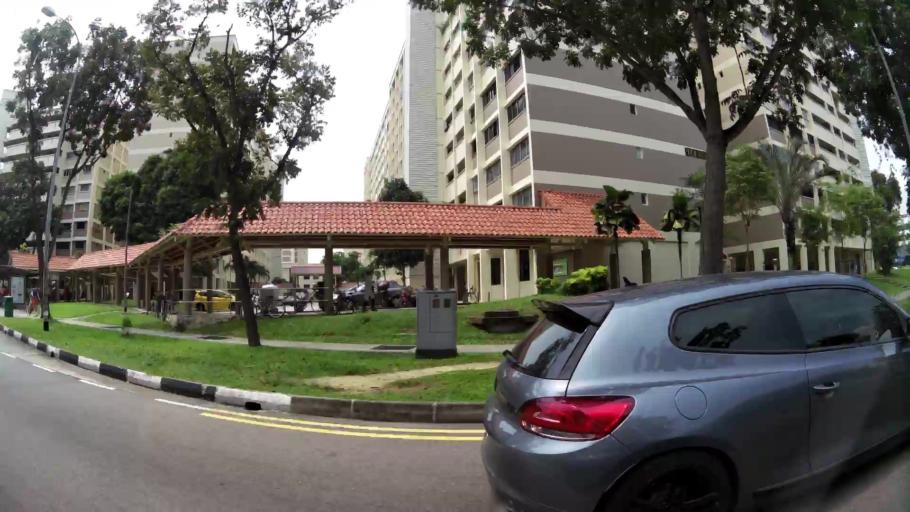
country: SG
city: Singapore
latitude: 1.3355
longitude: 103.9141
